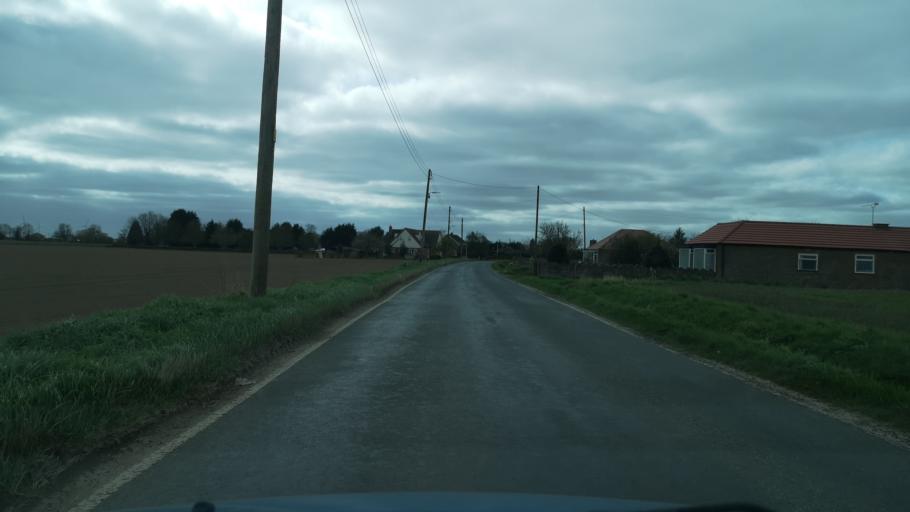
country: GB
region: England
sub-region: East Riding of Yorkshire
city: Skelton
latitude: 53.6942
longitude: -0.8222
